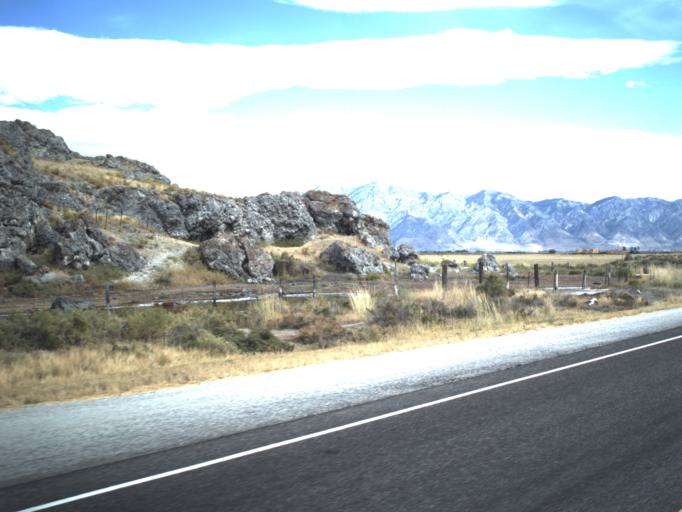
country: US
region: Utah
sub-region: Box Elder County
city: Elwood
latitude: 41.5767
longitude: -112.2343
